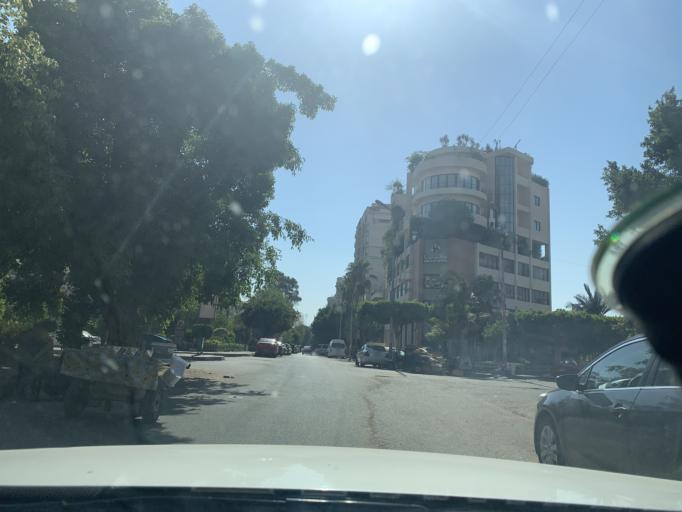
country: EG
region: Muhafazat al Qahirah
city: Cairo
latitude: 30.1128
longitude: 31.3381
